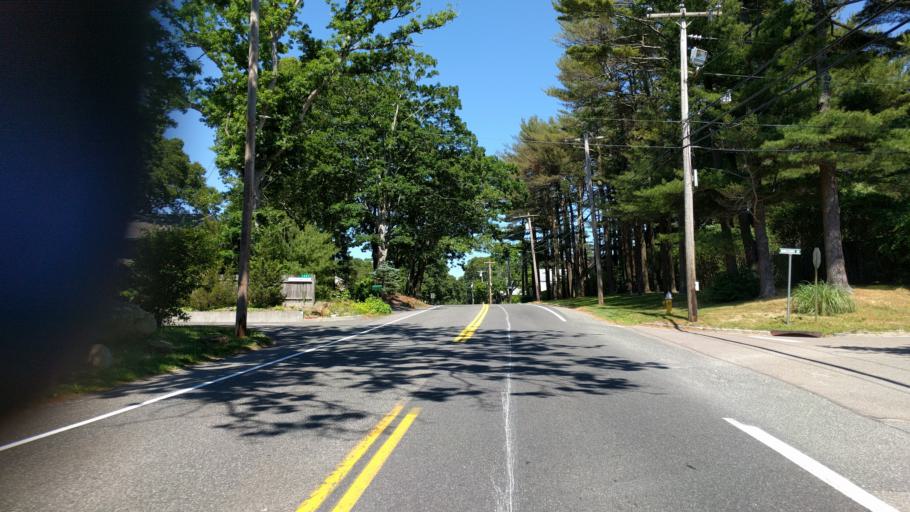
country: US
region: New York
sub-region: Suffolk County
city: Noyack
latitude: 40.9938
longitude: -72.3465
